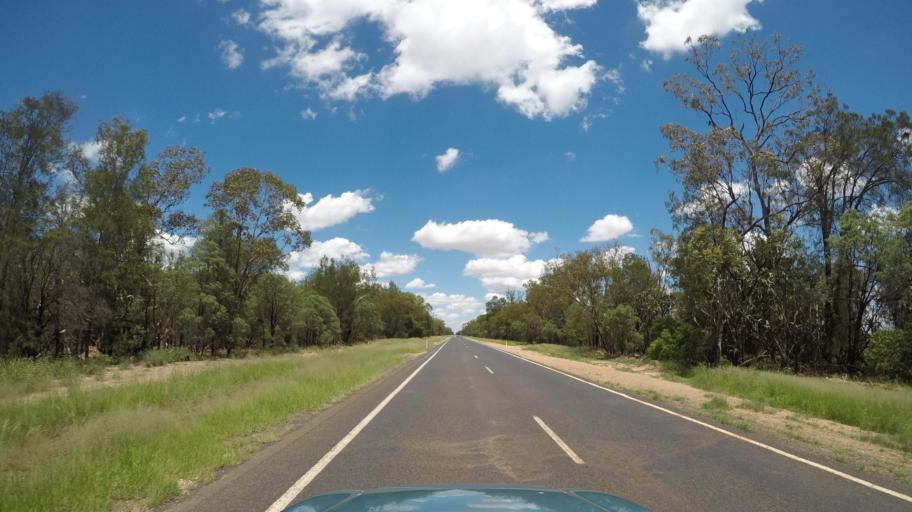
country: AU
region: Queensland
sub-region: Goondiwindi
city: Goondiwindi
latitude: -28.1613
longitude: 150.6265
